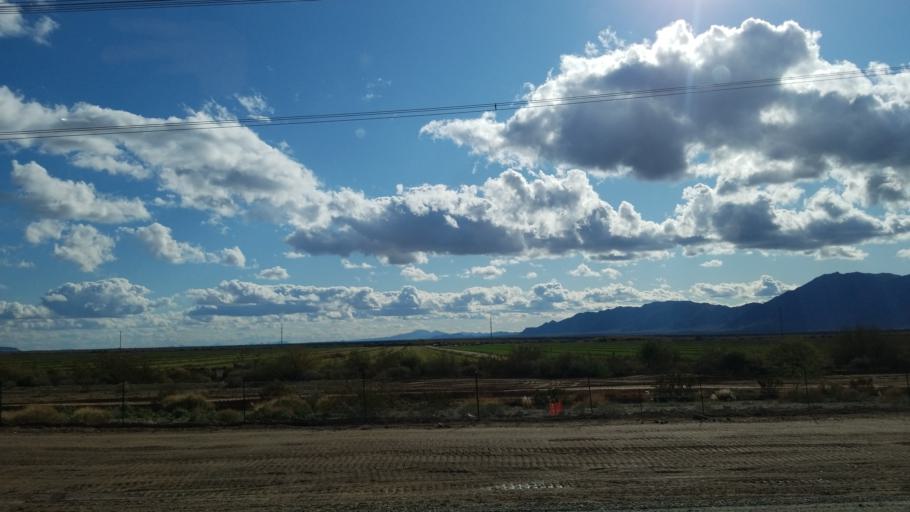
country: US
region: Arizona
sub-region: Maricopa County
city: Laveen
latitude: 33.2910
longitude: -112.1186
